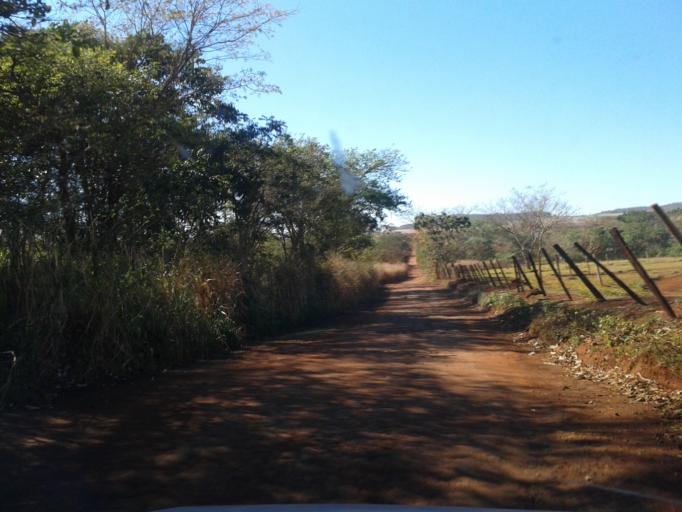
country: BR
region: Minas Gerais
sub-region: Centralina
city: Centralina
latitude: -18.5886
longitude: -49.1805
